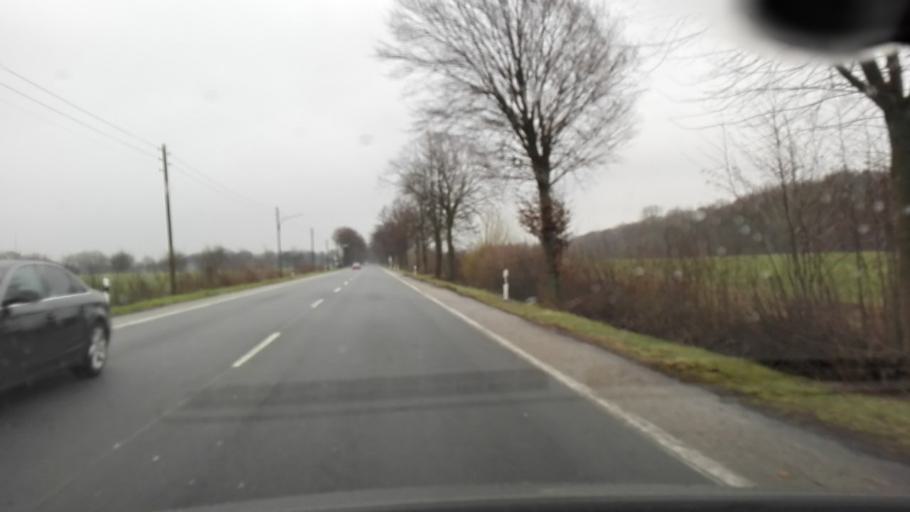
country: DE
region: North Rhine-Westphalia
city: Kamen
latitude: 51.5847
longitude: 7.6923
